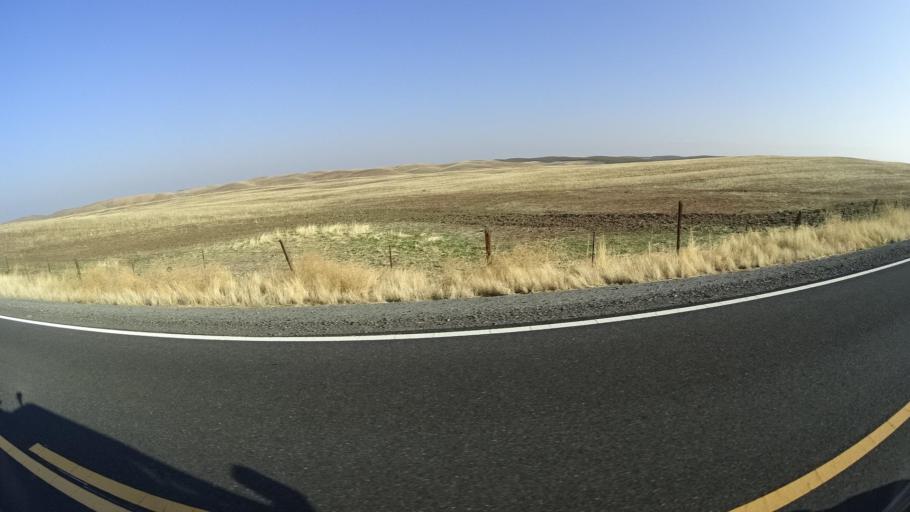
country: US
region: California
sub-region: Tulare County
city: Richgrove
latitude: 35.7551
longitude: -119.0178
